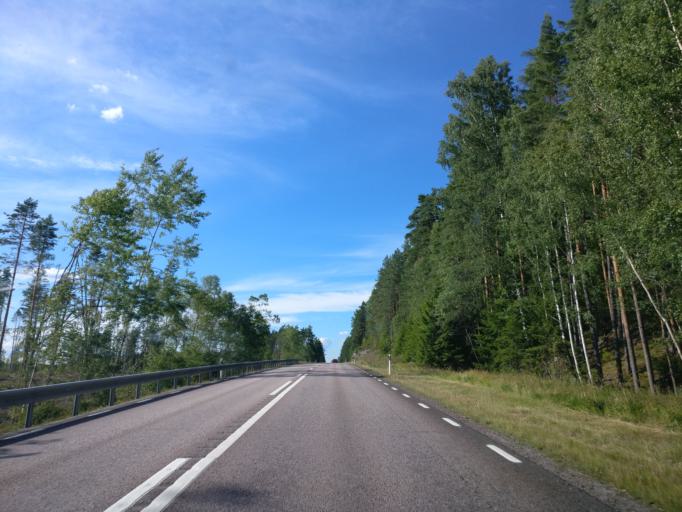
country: SE
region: Vaermland
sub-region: Karlstads Kommun
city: Edsvalla
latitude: 59.5838
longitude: 13.0148
